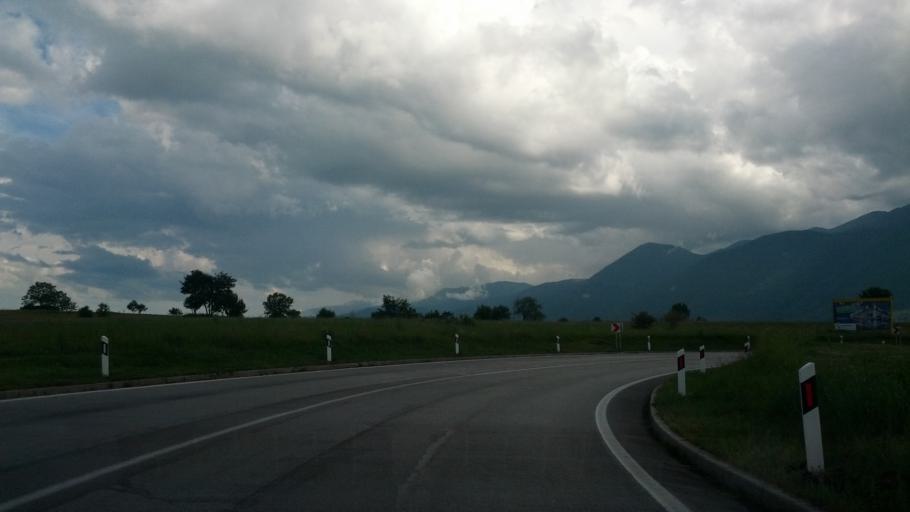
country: BA
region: Federation of Bosnia and Herzegovina
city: Izacic
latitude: 44.8732
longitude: 15.7700
